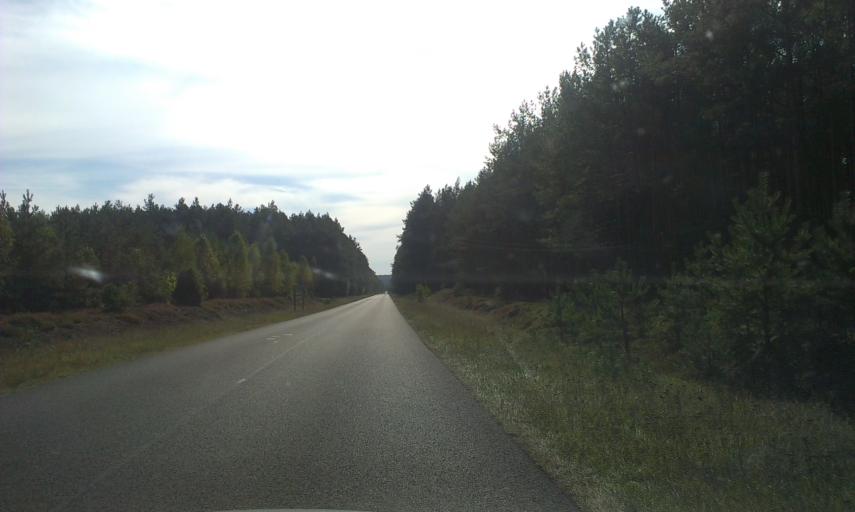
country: PL
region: Greater Poland Voivodeship
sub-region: Powiat zlotowski
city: Okonek
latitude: 53.5141
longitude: 16.9748
